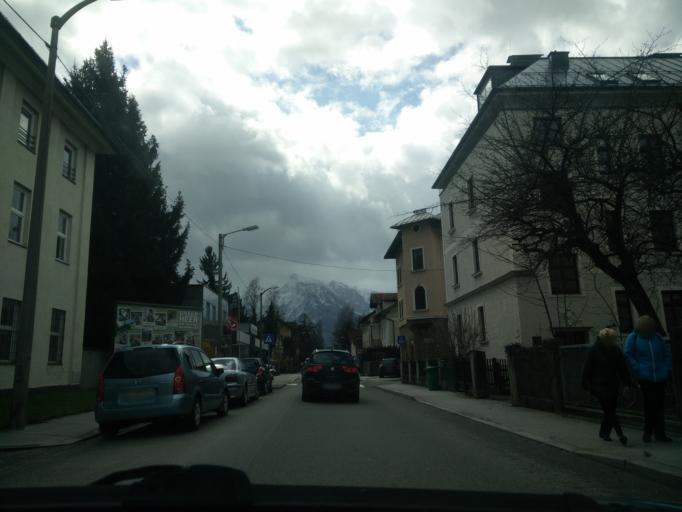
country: AT
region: Salzburg
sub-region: Salzburg Stadt
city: Salzburg
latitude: 47.7959
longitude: 13.0301
